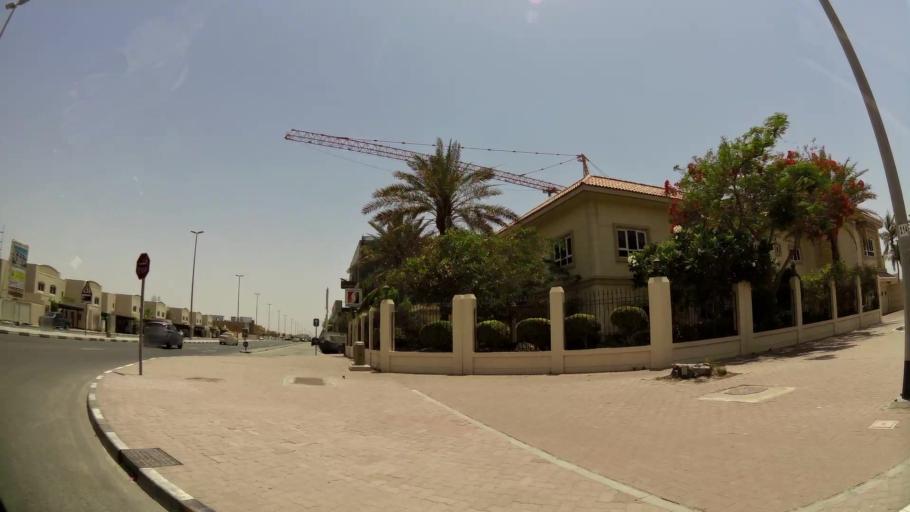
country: AE
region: Dubai
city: Dubai
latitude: 25.2242
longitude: 55.2652
